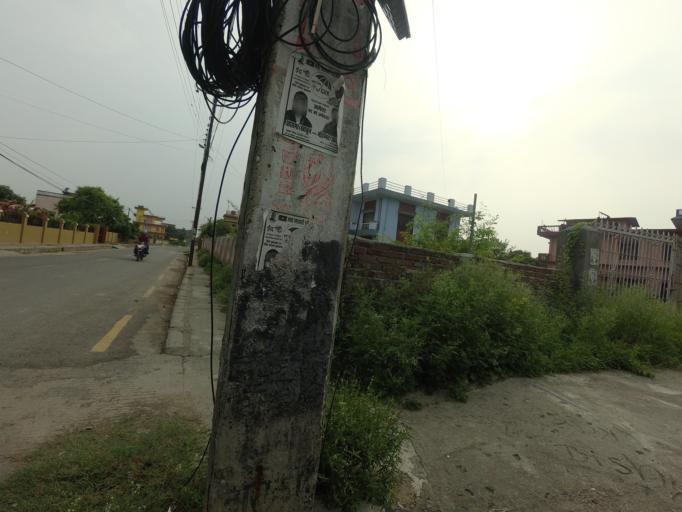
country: NP
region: Western Region
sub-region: Lumbini Zone
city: Bhairahawa
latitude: 27.4915
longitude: 83.4462
